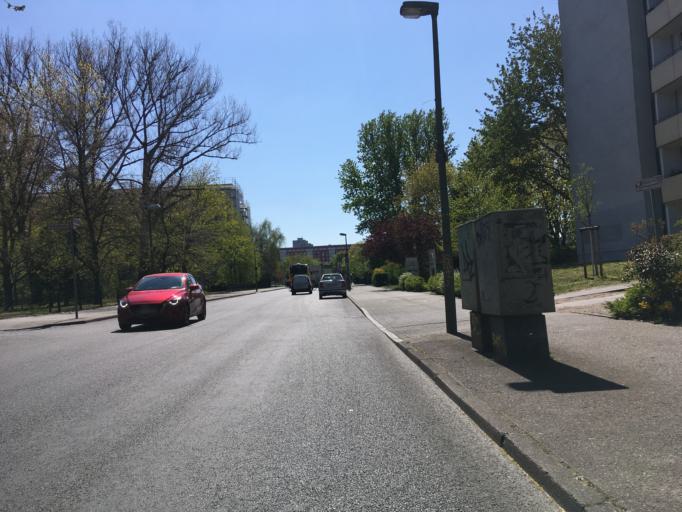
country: DE
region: Berlin
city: Friedrichsfelde
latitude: 52.5009
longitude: 13.5088
